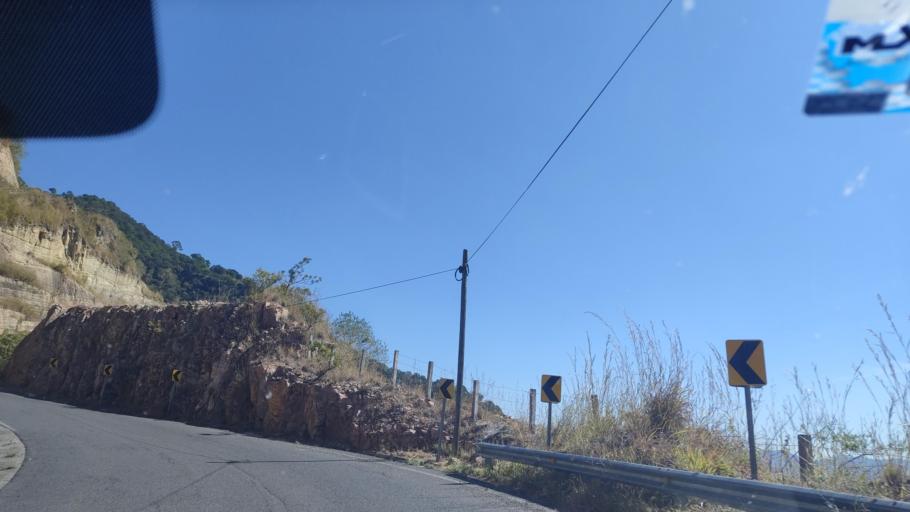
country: MX
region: Nayarit
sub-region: Jala
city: Rosa Blanca
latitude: 21.0921
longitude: -104.3823
